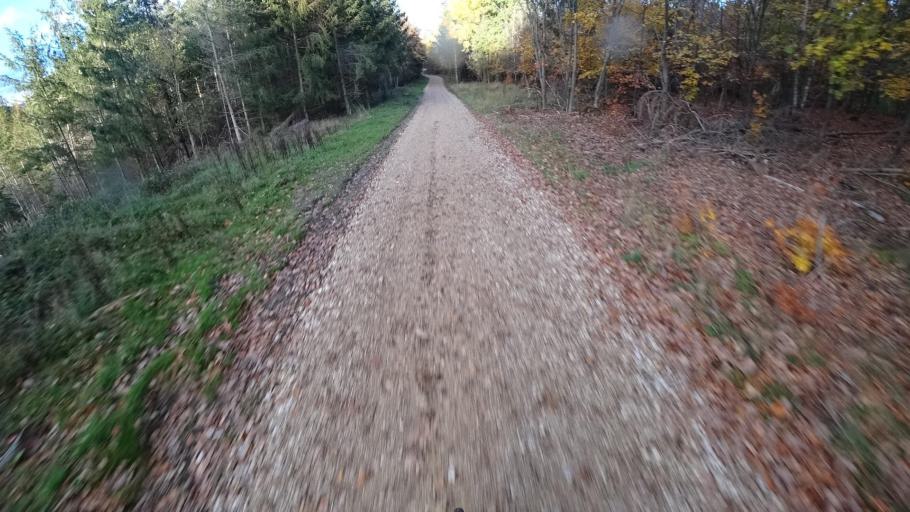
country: DE
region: Rheinland-Pfalz
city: Sierscheid
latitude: 50.4663
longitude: 6.9070
